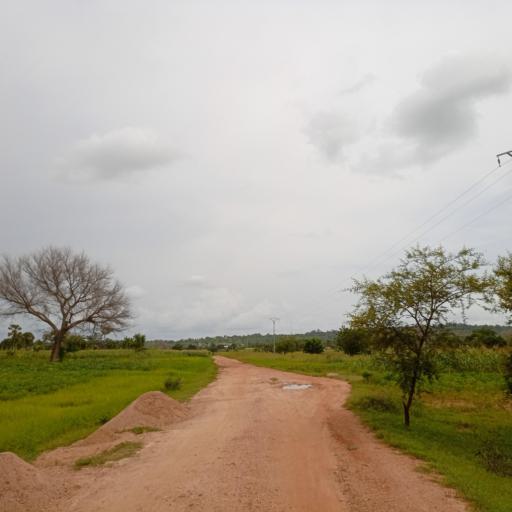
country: TG
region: Savanes
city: Dapaong
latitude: 10.8084
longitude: 0.0275
